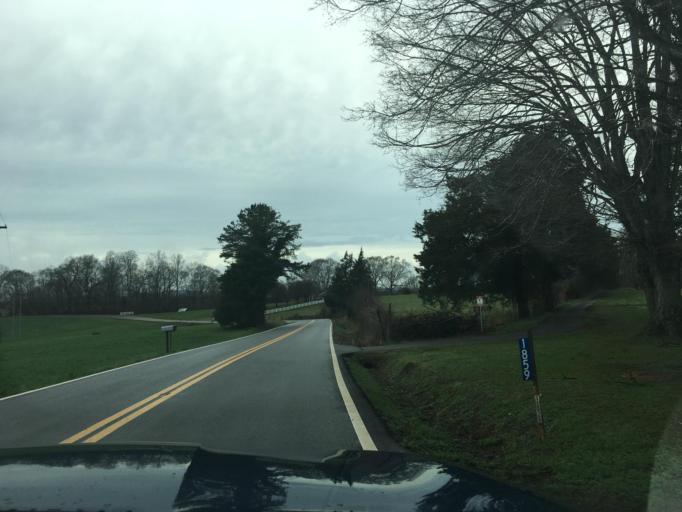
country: US
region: Tennessee
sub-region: McMinn County
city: Englewood
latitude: 35.4196
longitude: -84.4676
